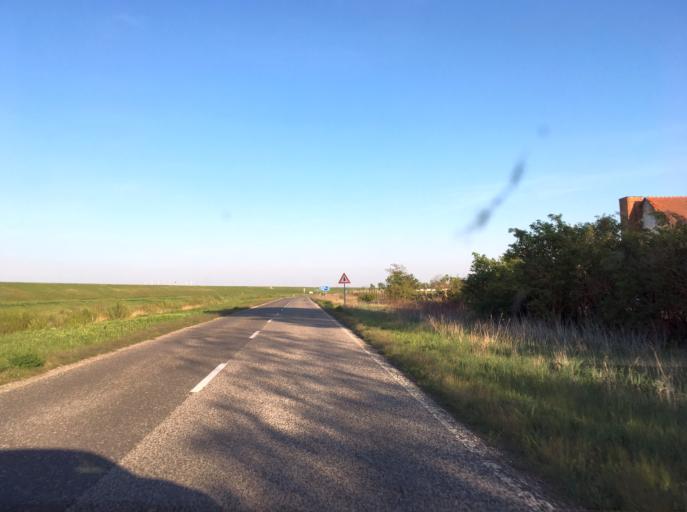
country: SK
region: Trnavsky
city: Samorin
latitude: 47.9890
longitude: 17.3612
